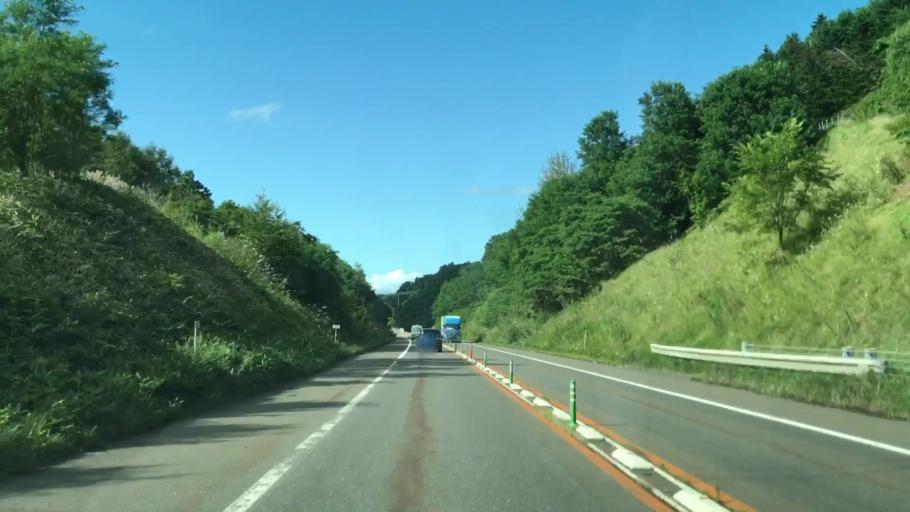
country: JP
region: Hokkaido
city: Date
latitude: 42.4553
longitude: 140.9127
